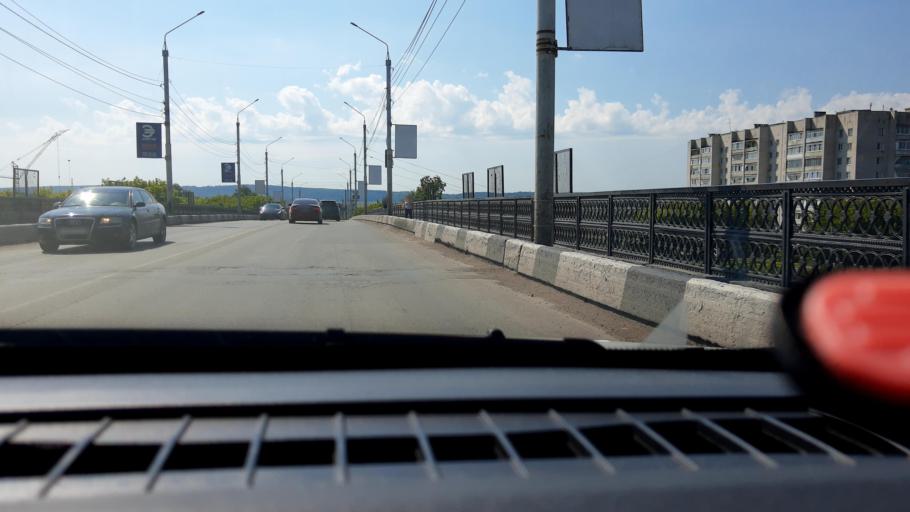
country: RU
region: Nizjnij Novgorod
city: Dzerzhinsk
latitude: 56.2351
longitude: 43.4889
